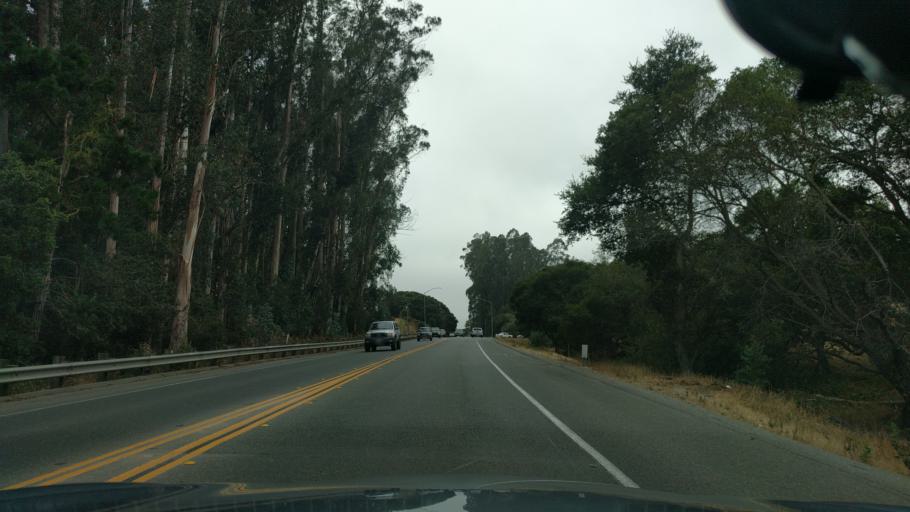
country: US
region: California
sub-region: Monterey County
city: Prunedale
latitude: 36.7884
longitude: -121.6769
